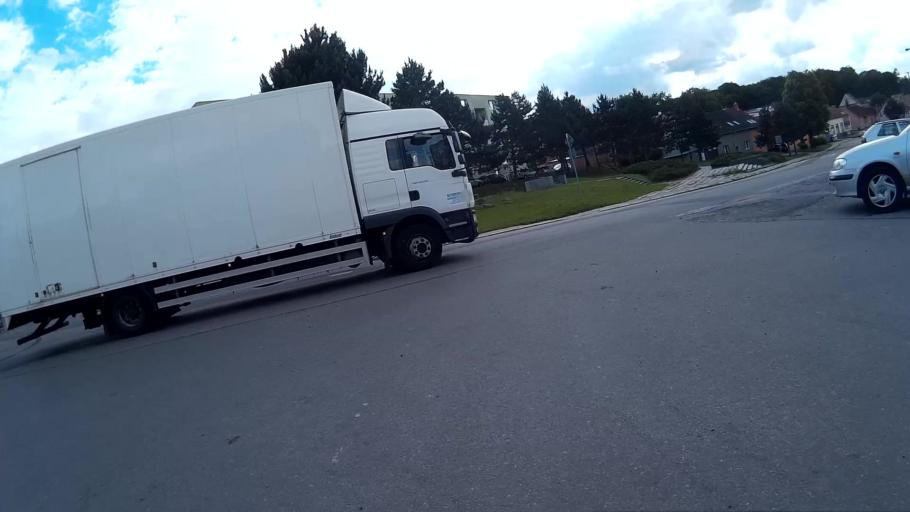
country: CZ
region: South Moravian
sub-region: Okres Brno-Venkov
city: Rosice
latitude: 49.1834
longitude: 16.3920
